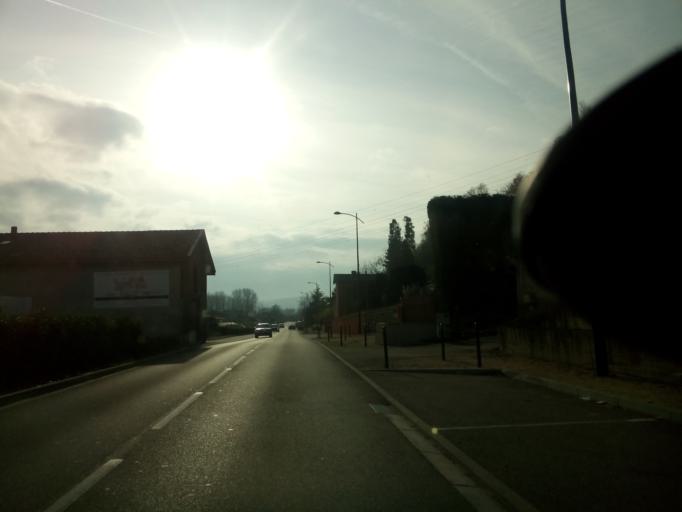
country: FR
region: Rhone-Alpes
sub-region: Departement de la Loire
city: Chavanay
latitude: 45.4267
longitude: 4.7404
